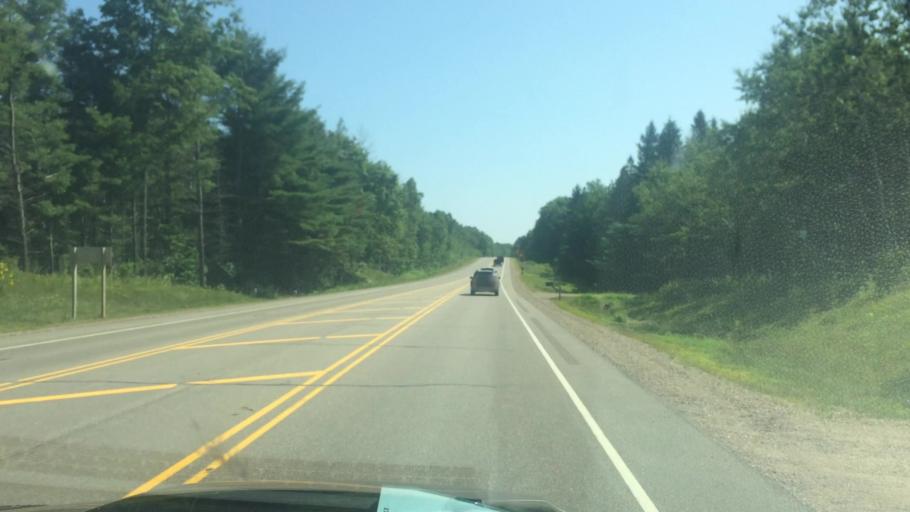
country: US
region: Wisconsin
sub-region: Oneida County
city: Rhinelander
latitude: 45.6136
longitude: -89.5374
